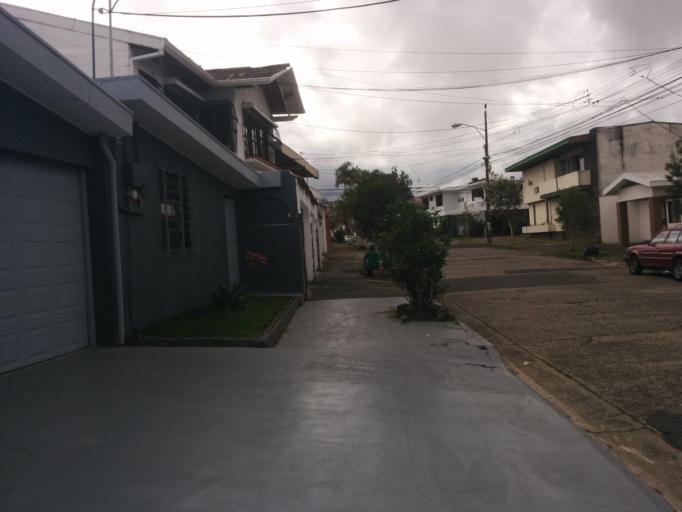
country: CR
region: San Jose
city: San Pedro
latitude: 9.9280
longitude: -84.0618
